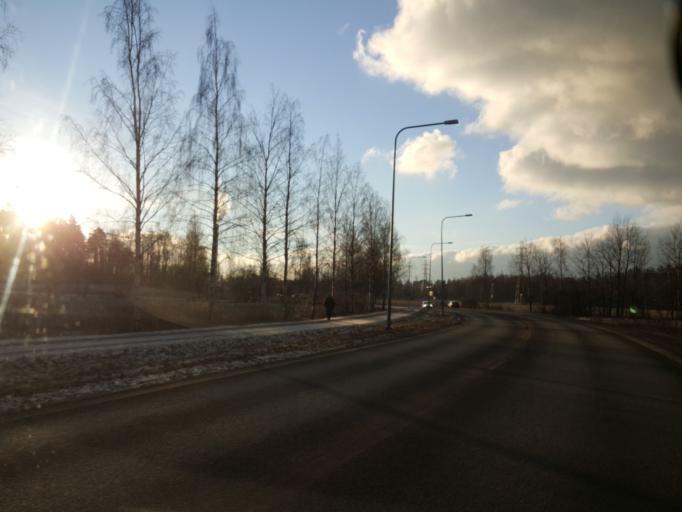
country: FI
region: Uusimaa
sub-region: Helsinki
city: Vantaa
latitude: 60.2481
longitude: 24.9770
